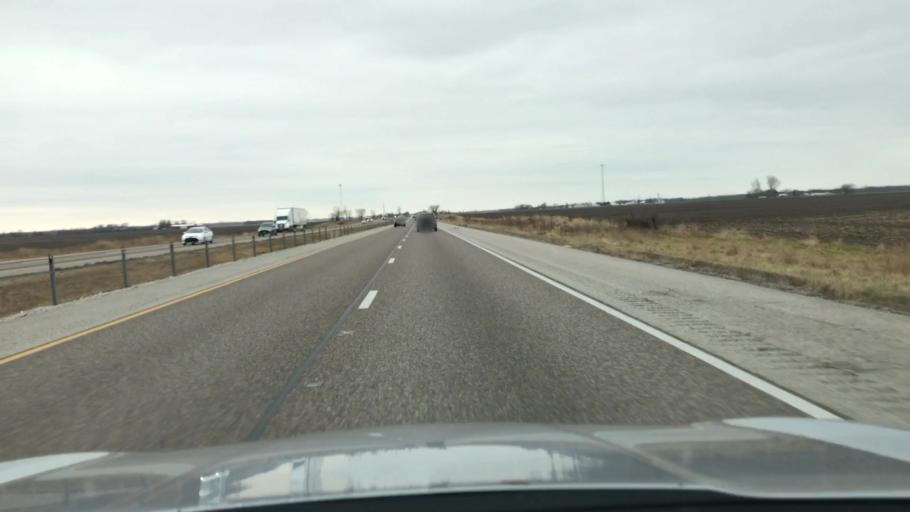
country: US
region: Illinois
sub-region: Madison County
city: Worden
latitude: 38.8462
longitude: -89.8684
